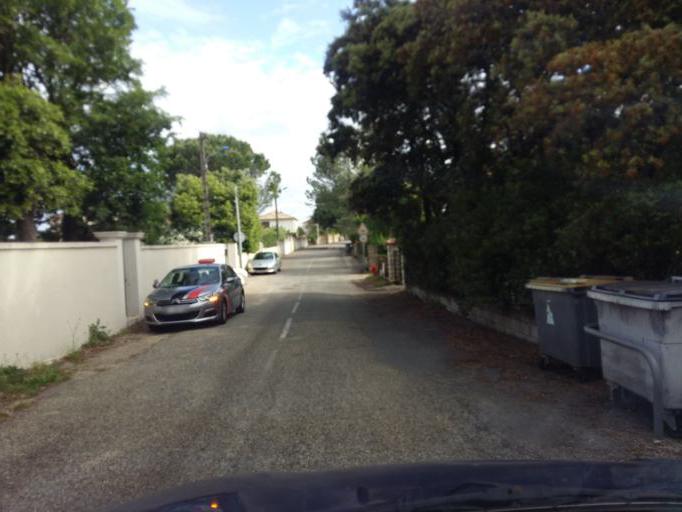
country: FR
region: Languedoc-Roussillon
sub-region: Departement du Gard
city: Bagnols-sur-Ceze
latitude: 44.1477
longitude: 4.6132
